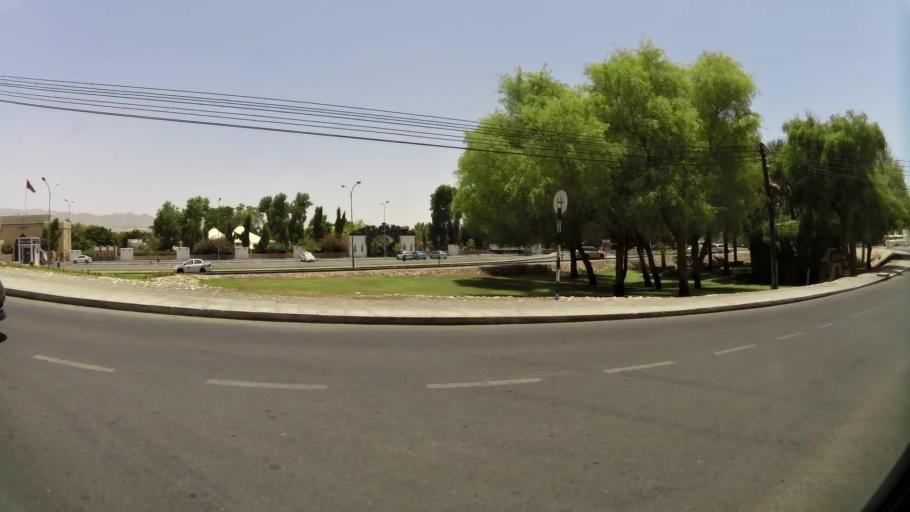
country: OM
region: Muhafazat Masqat
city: Muscat
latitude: 23.6225
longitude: 58.4928
